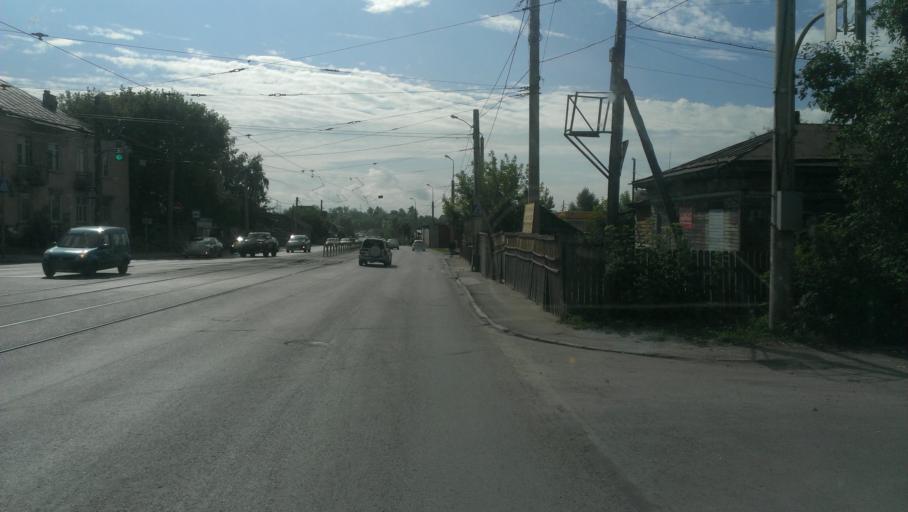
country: RU
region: Altai Krai
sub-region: Gorod Barnaulskiy
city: Barnaul
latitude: 53.3443
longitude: 83.7338
